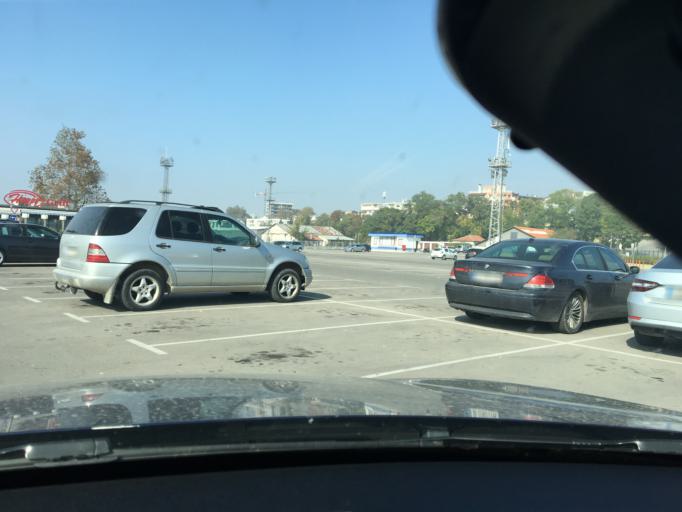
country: BG
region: Varna
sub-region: Obshtina Varna
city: Varna
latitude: 43.1958
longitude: 27.9207
